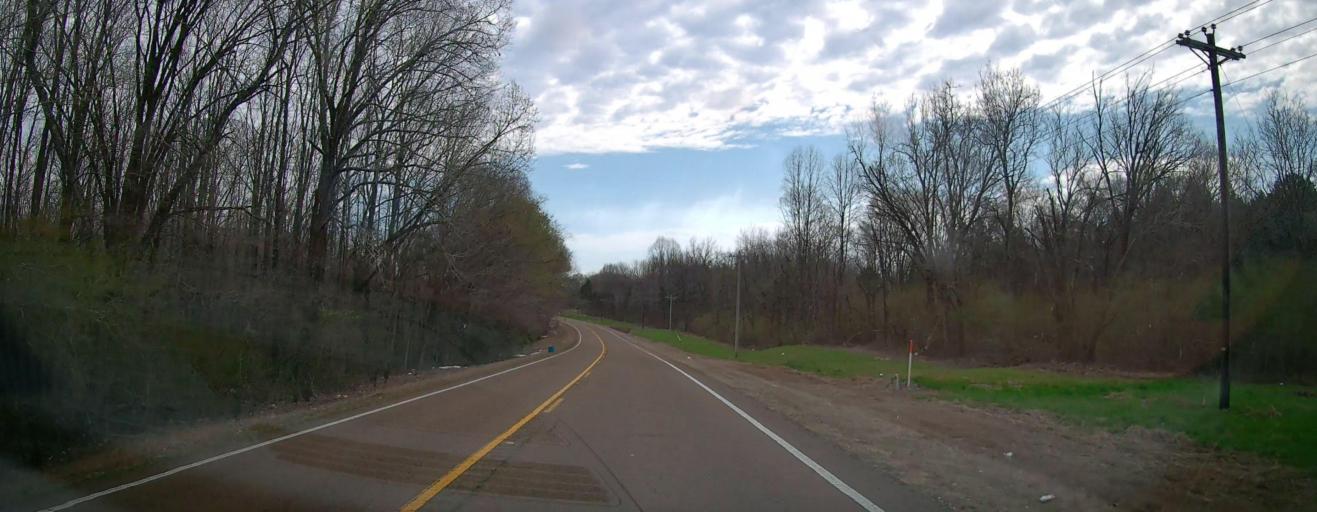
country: US
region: Mississippi
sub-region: Marshall County
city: Byhalia
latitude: 34.8494
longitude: -89.6290
